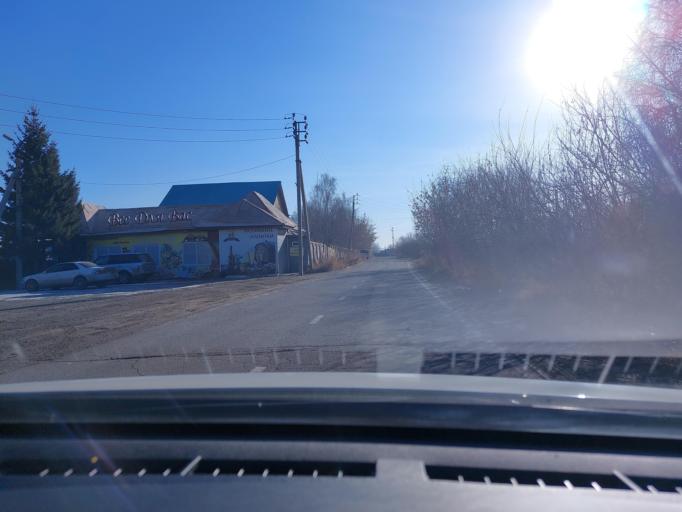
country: RU
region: Irkutsk
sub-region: Irkutskiy Rayon
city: Irkutsk
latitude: 52.3102
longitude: 104.2713
